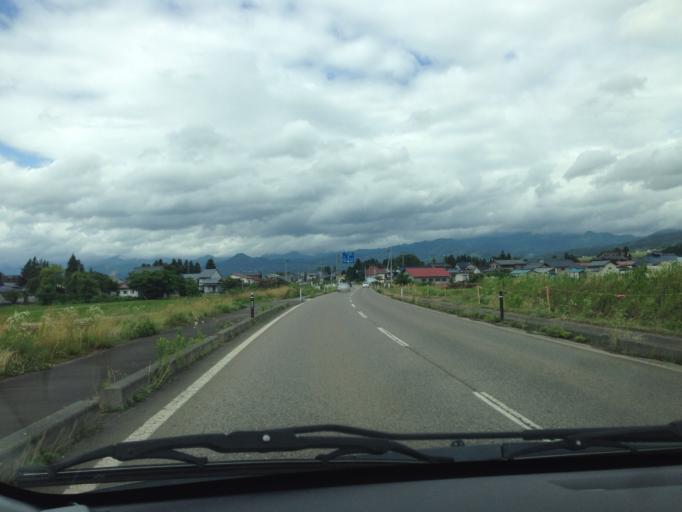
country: JP
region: Fukushima
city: Kitakata
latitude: 37.6079
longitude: 139.9114
